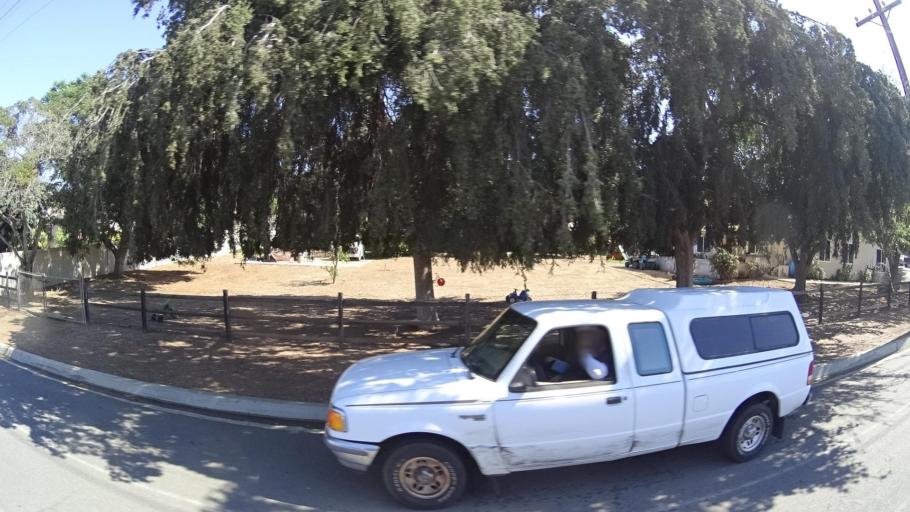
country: US
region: California
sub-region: San Diego County
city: Granite Hills
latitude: 32.7967
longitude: -116.9025
